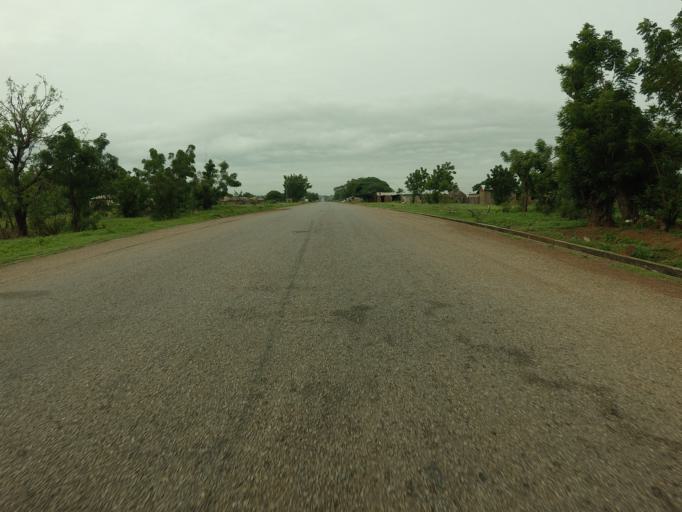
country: GH
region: Northern
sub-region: Yendi
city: Yendi
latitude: 9.5046
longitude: -0.0269
